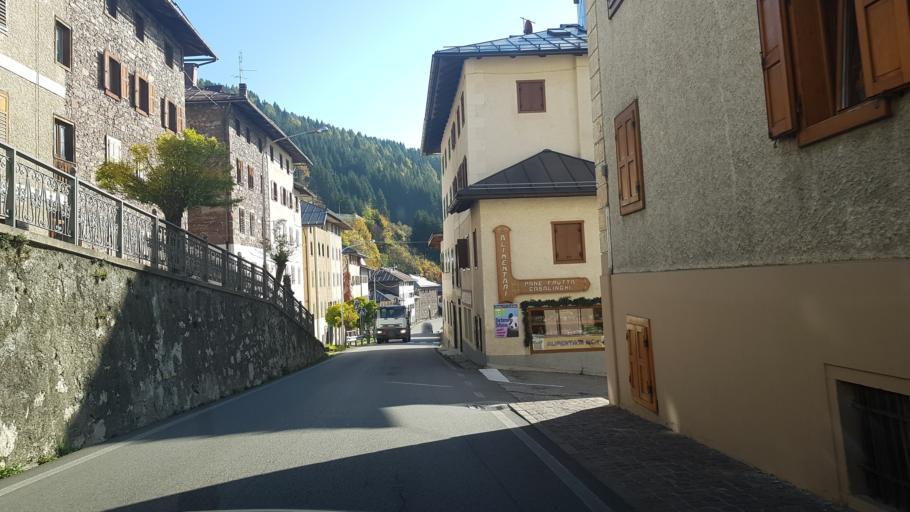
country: IT
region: Veneto
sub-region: Provincia di Belluno
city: Candide
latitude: 46.5995
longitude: 12.4925
